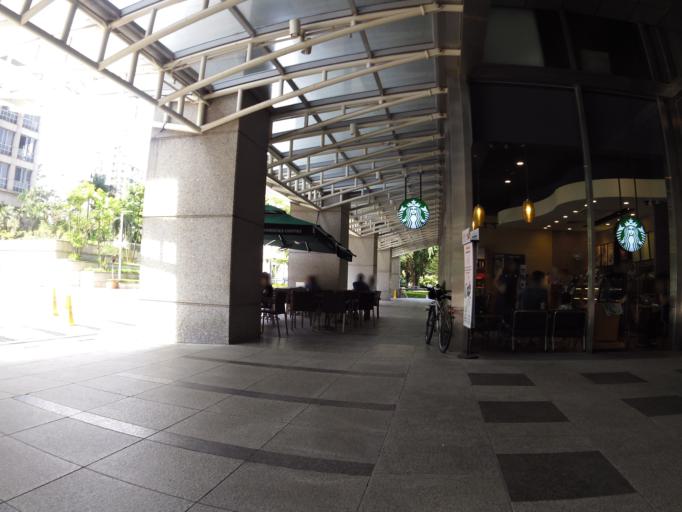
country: SG
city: Singapore
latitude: 1.2928
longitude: 103.8427
